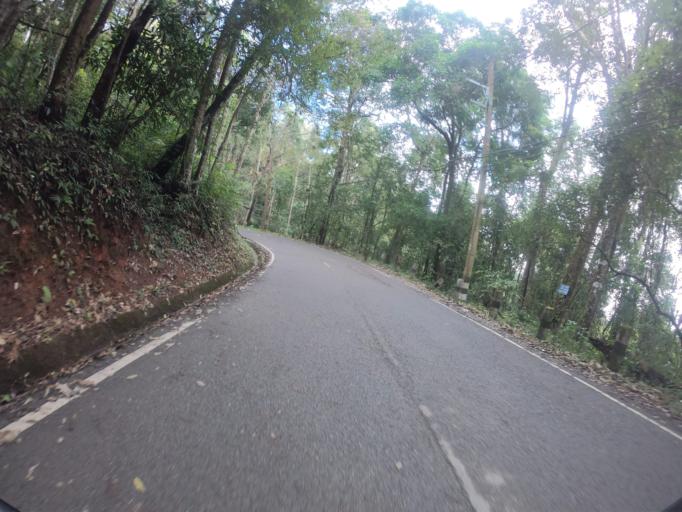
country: TH
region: Chiang Mai
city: Chiang Mai
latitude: 18.8086
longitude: 98.8944
